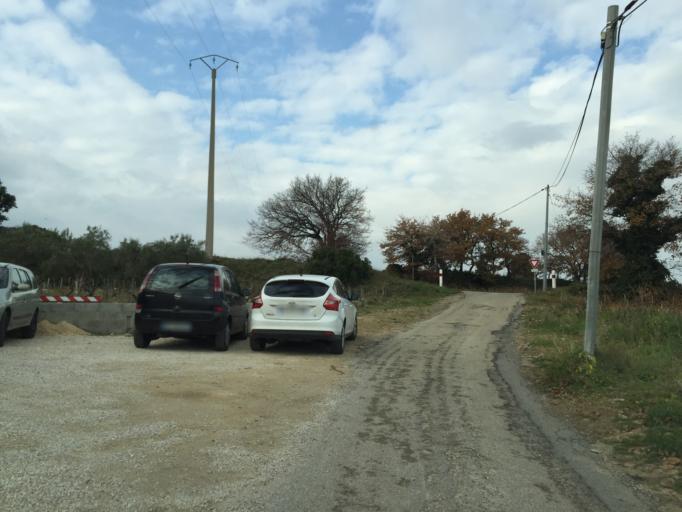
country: FR
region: Provence-Alpes-Cote d'Azur
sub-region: Departement du Vaucluse
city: Bedarrides
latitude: 44.0467
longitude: 4.8811
